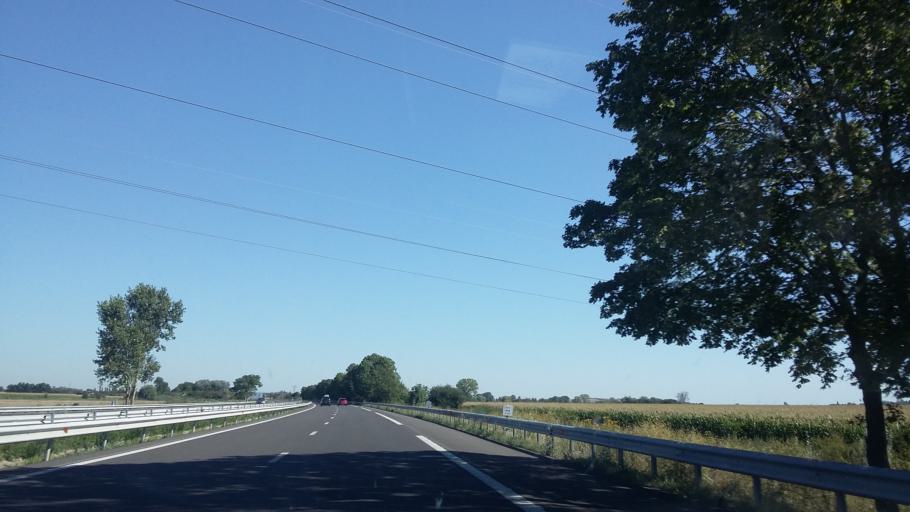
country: FR
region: Auvergne
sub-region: Departement du Puy-de-Dome
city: Pont-du-Chateau
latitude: 45.8087
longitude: 3.2205
